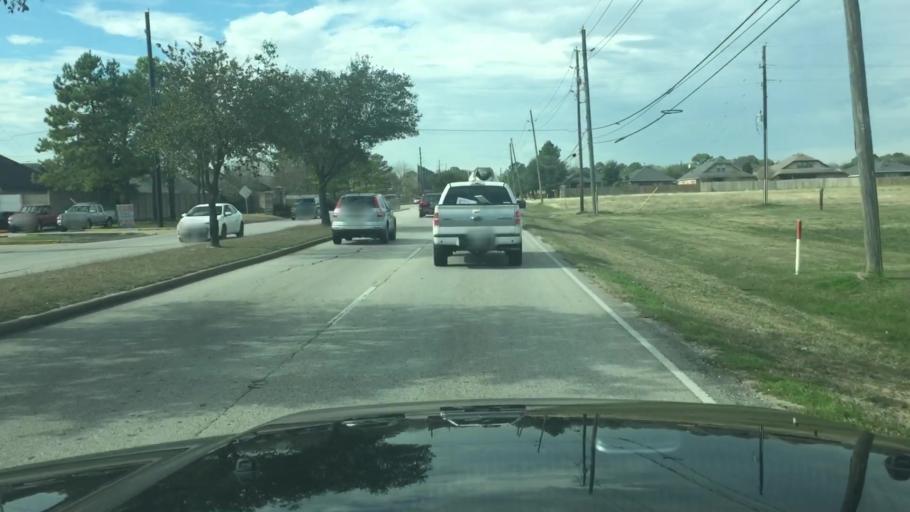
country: US
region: Texas
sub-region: Harris County
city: Oak Cliff Place
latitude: 29.8311
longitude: -95.6708
